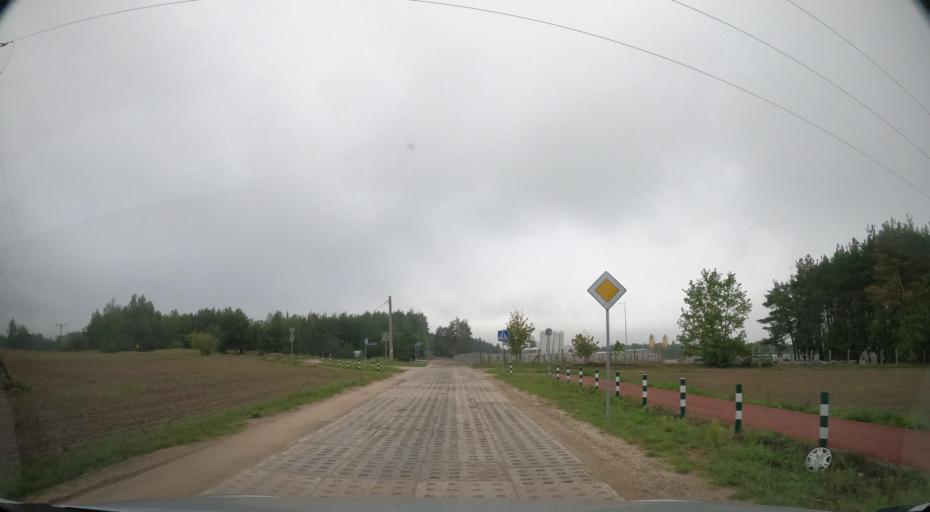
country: PL
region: Pomeranian Voivodeship
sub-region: Powiat kartuski
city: Chwaszczyno
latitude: 54.4272
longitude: 18.4158
